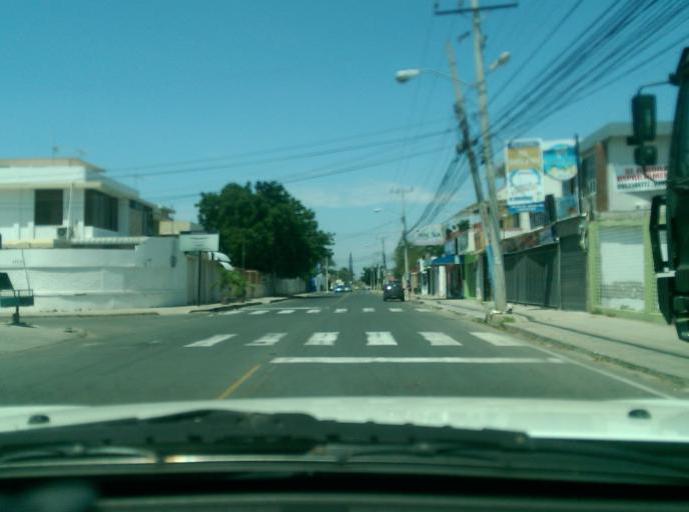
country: EC
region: Manabi
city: Manta
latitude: -0.9573
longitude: -80.7529
